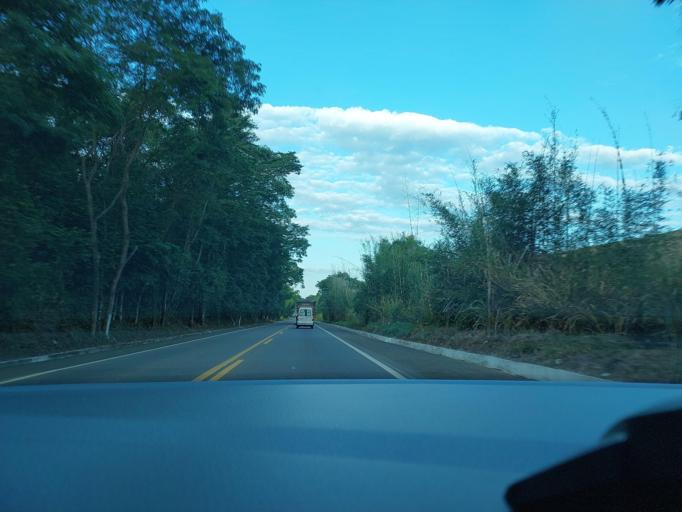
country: BR
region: Minas Gerais
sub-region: Muriae
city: Muriae
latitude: -21.1355
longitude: -42.1855
